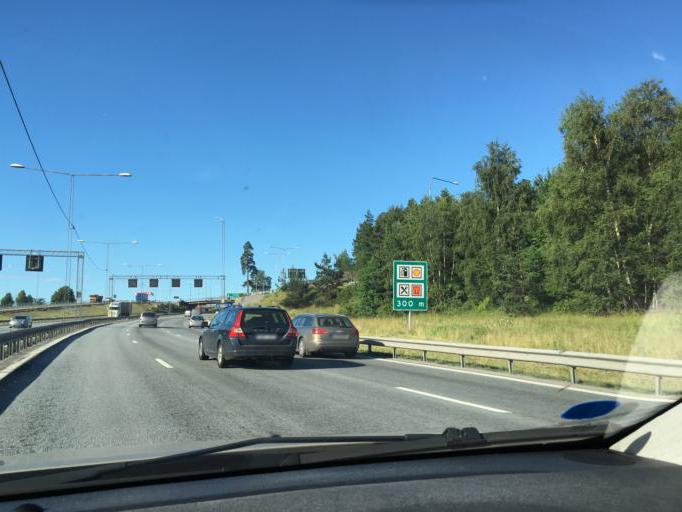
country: SE
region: Stockholm
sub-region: Botkyrka Kommun
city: Alby
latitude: 59.2426
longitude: 17.8386
